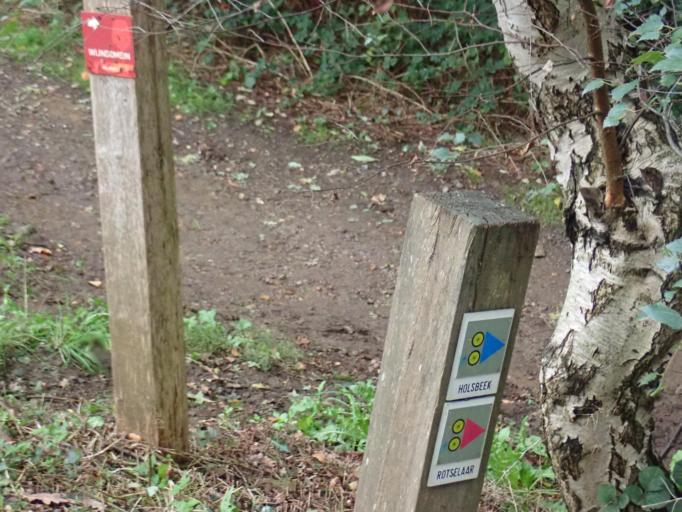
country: BE
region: Flanders
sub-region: Provincie Vlaams-Brabant
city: Aarschot
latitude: 50.9481
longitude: 4.8048
